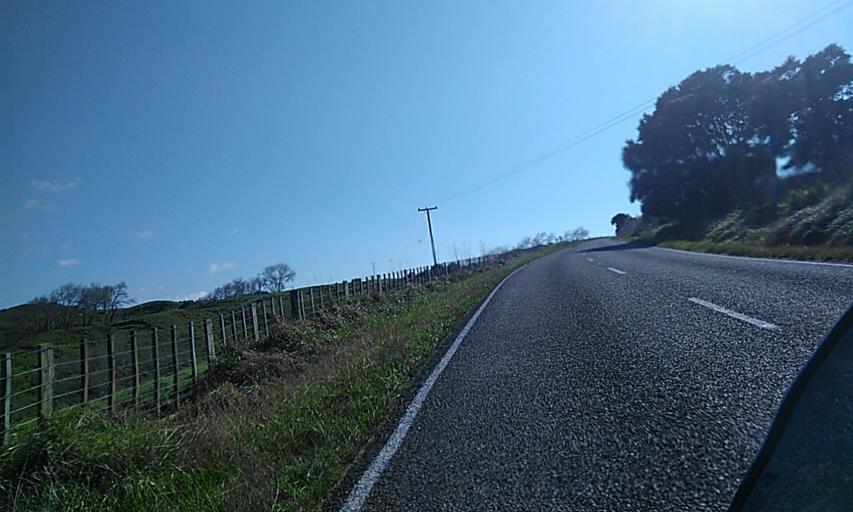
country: NZ
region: Gisborne
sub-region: Gisborne District
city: Gisborne
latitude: -38.4959
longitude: 178.0573
